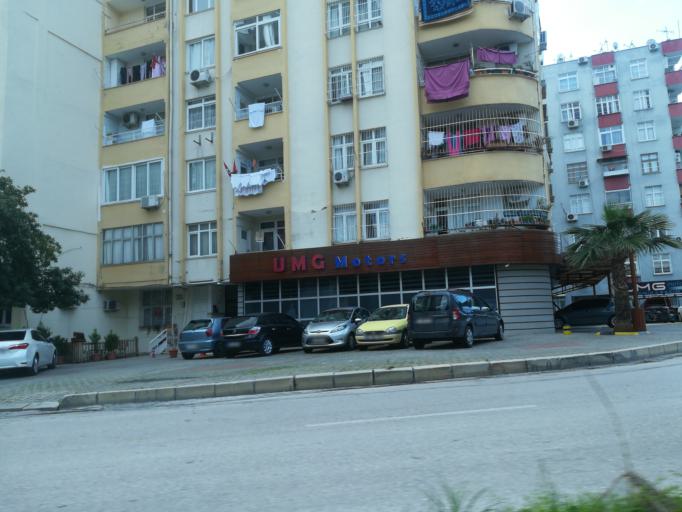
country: TR
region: Adana
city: Adana
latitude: 37.0313
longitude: 35.3066
